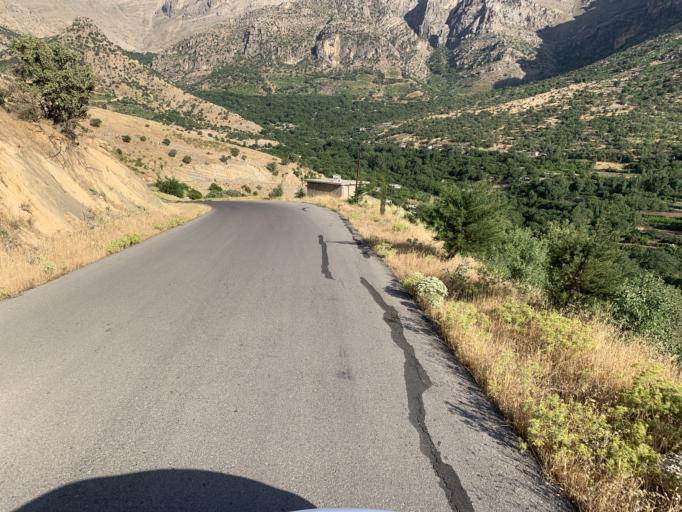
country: IQ
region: As Sulaymaniyah
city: Qeladize
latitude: 35.9950
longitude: 45.1927
